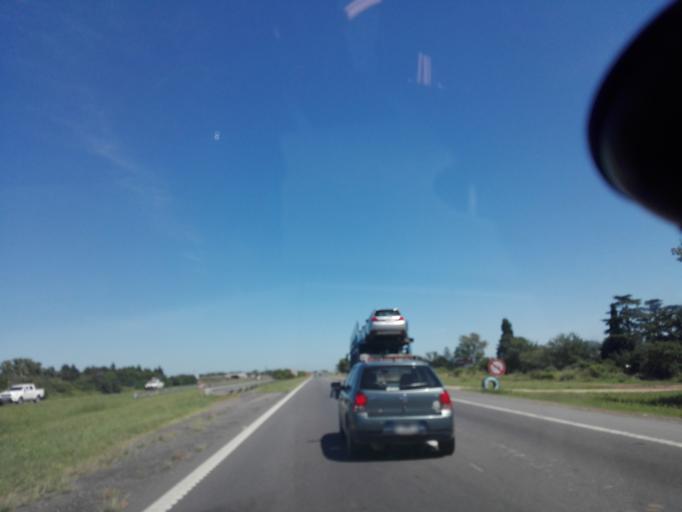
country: AR
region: Buenos Aires
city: San Nicolas de los Arroyos
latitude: -33.3845
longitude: -60.2272
